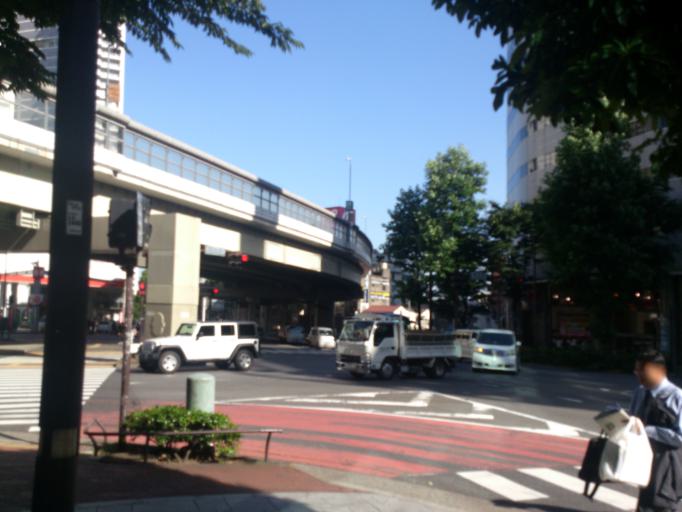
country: JP
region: Tokyo
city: Tokyo
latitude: 35.7276
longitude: 139.7165
